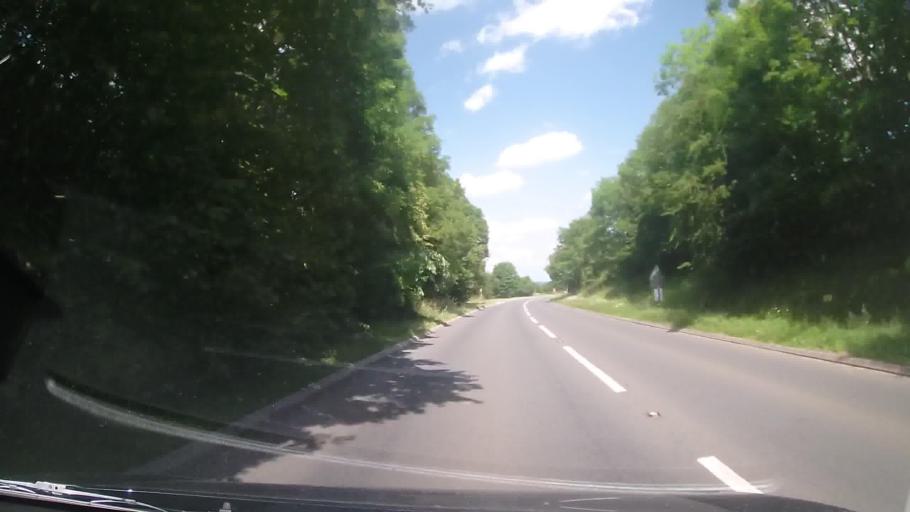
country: GB
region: England
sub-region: Herefordshire
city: Ocle Pychard
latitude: 52.0894
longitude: -2.5840
